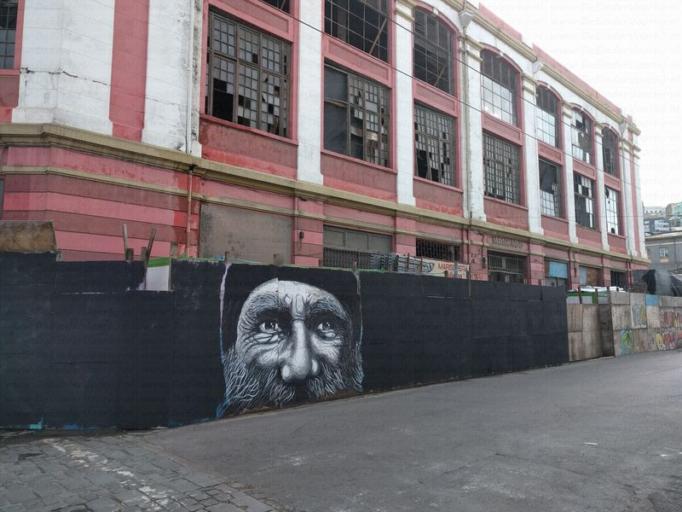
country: CL
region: Valparaiso
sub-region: Provincia de Valparaiso
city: Valparaiso
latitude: -33.0363
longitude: -71.6295
